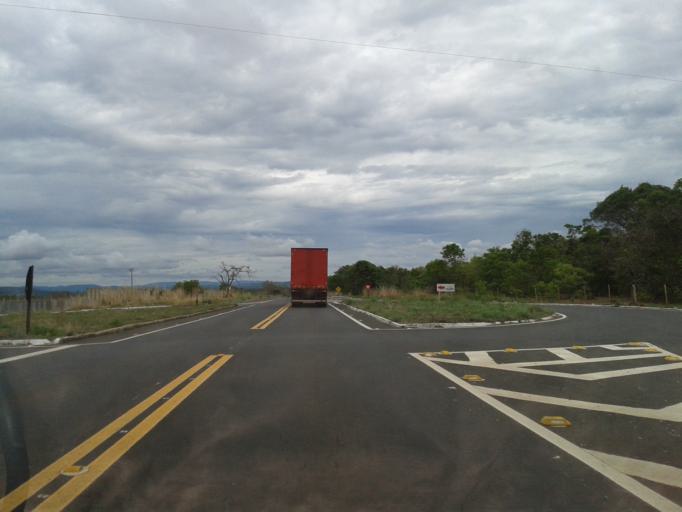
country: BR
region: Goias
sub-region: Caldas Novas
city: Caldas Novas
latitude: -17.8461
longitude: -48.6361
